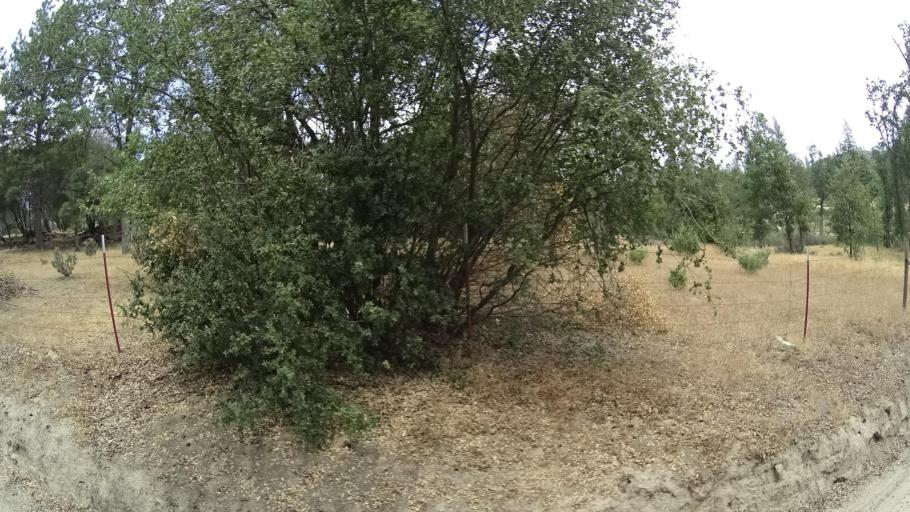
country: US
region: California
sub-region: Madera County
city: Ahwahnee
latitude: 37.4388
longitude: -119.8221
